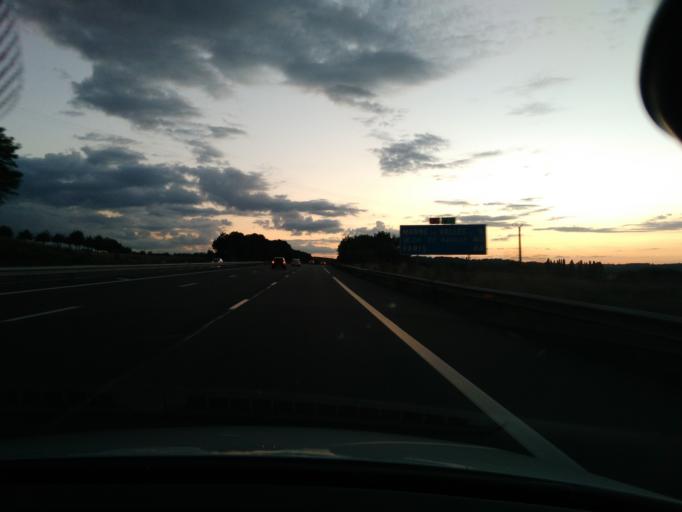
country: FR
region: Ile-de-France
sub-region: Departement de Seine-et-Marne
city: Villiers-sur-Morin
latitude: 48.8789
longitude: 2.8825
